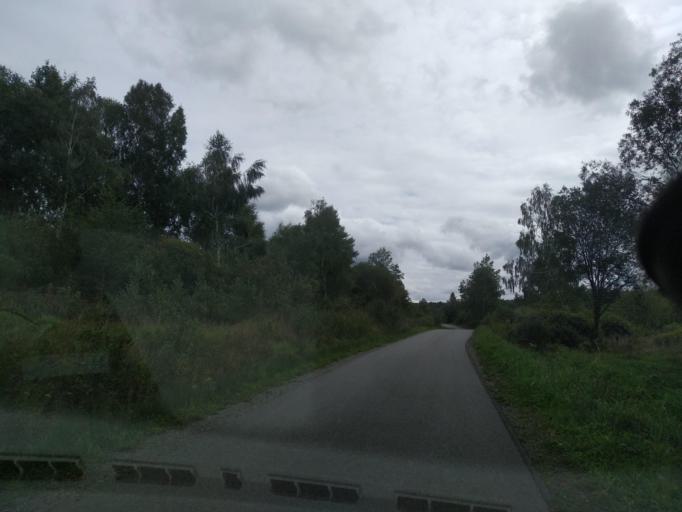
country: PL
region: Lesser Poland Voivodeship
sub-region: Powiat gorlicki
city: Uscie Gorlickie
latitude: 49.5425
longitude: 21.1946
